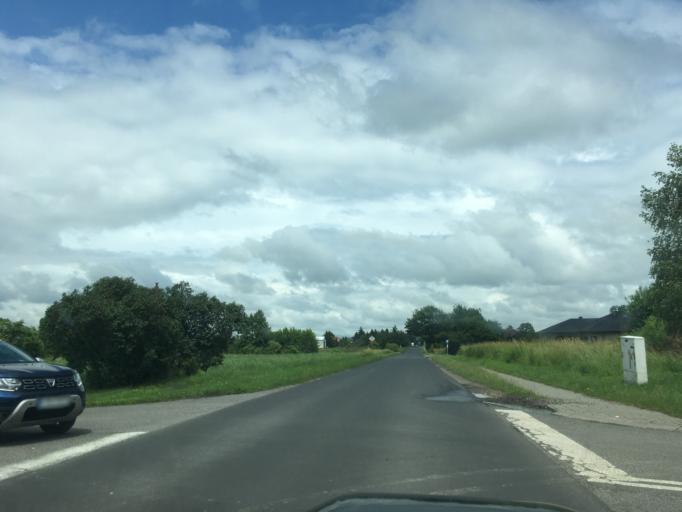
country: PL
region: Lublin Voivodeship
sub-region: Powiat swidnicki
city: Melgiew
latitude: 51.2106
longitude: 22.7451
